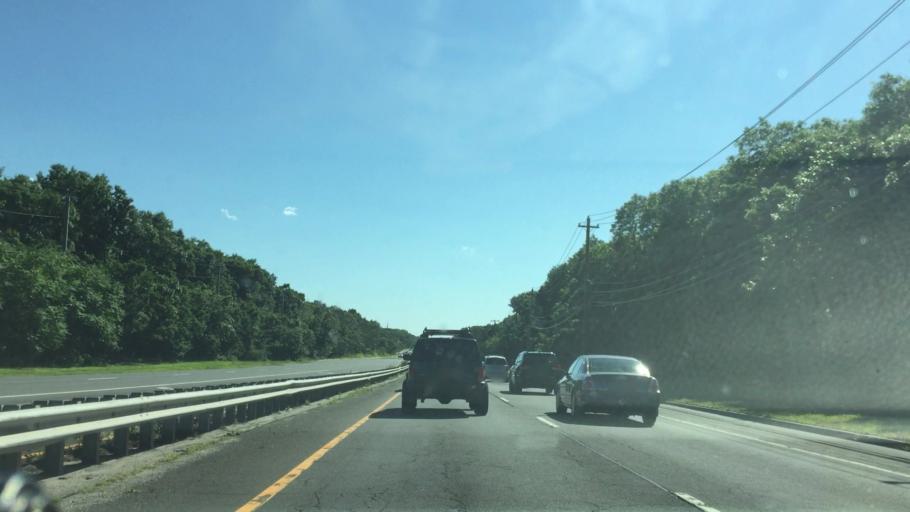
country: US
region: New York
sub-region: Suffolk County
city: Terryville
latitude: 40.8940
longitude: -73.0891
